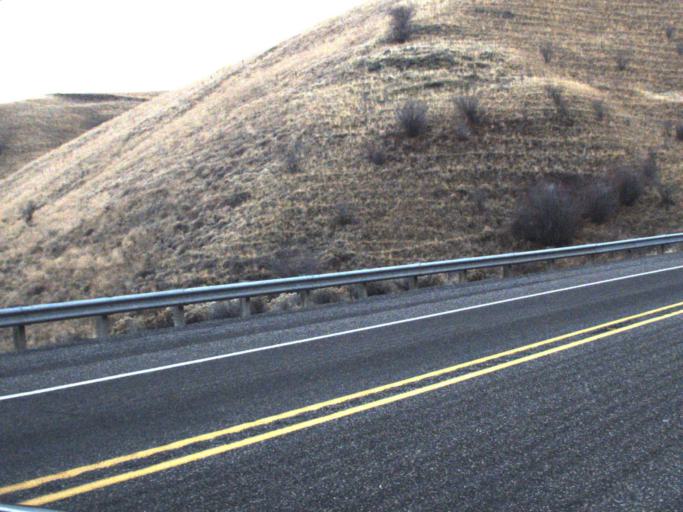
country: US
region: Washington
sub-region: Garfield County
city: Pomeroy
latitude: 46.4413
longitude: -117.3933
